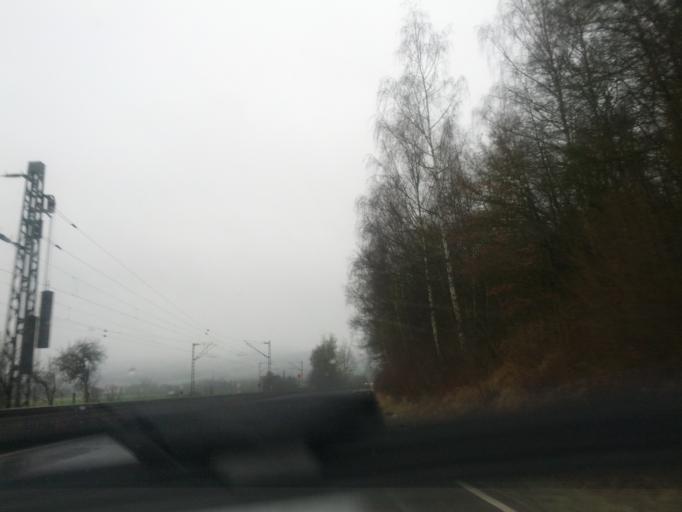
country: DE
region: Hesse
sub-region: Regierungsbezirk Kassel
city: Eschwege
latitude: 51.1689
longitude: 9.9902
